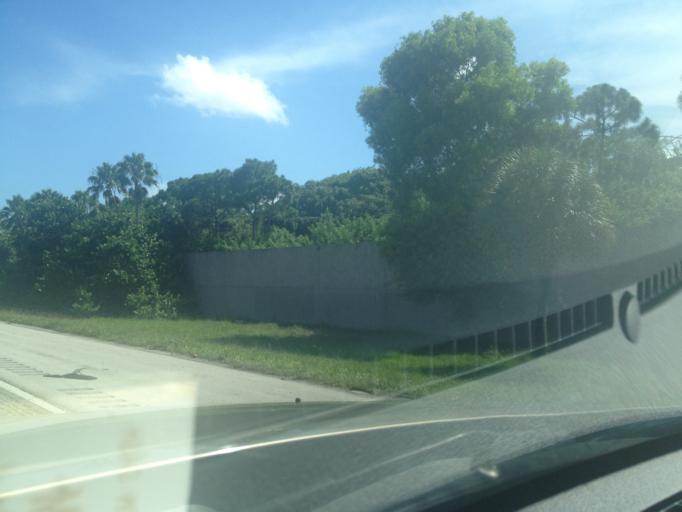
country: US
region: Florida
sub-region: Broward County
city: Deerfield Beach
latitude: 26.3370
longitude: -80.1178
